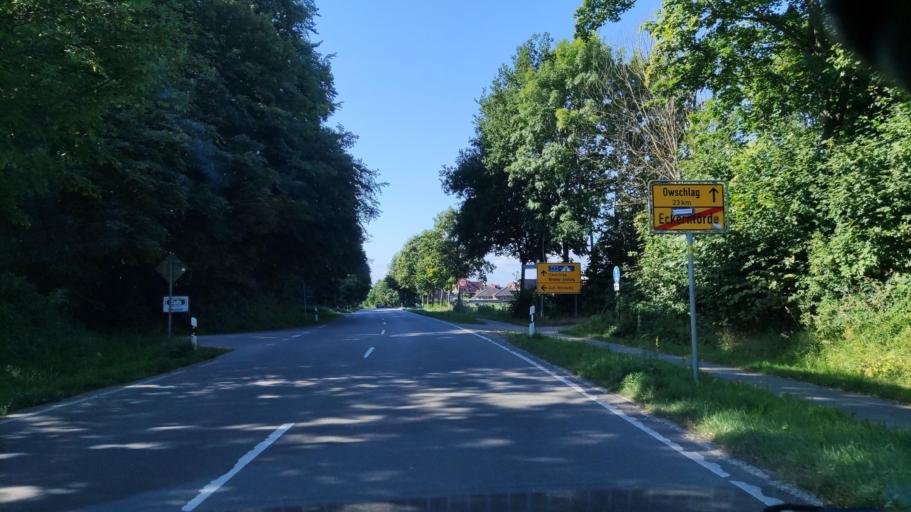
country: DE
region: Schleswig-Holstein
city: Windeby
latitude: 54.4621
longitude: 9.8208
